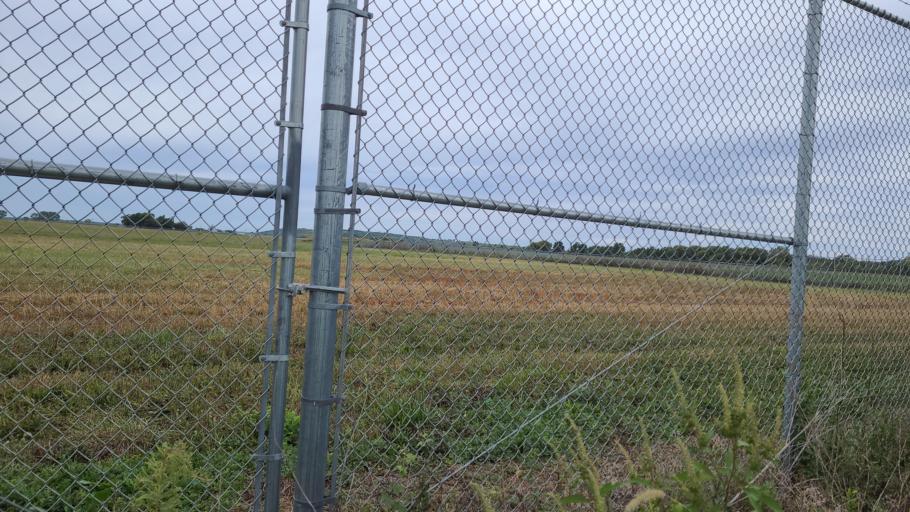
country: US
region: Kansas
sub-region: Douglas County
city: Lawrence
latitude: 39.0152
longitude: -95.2141
